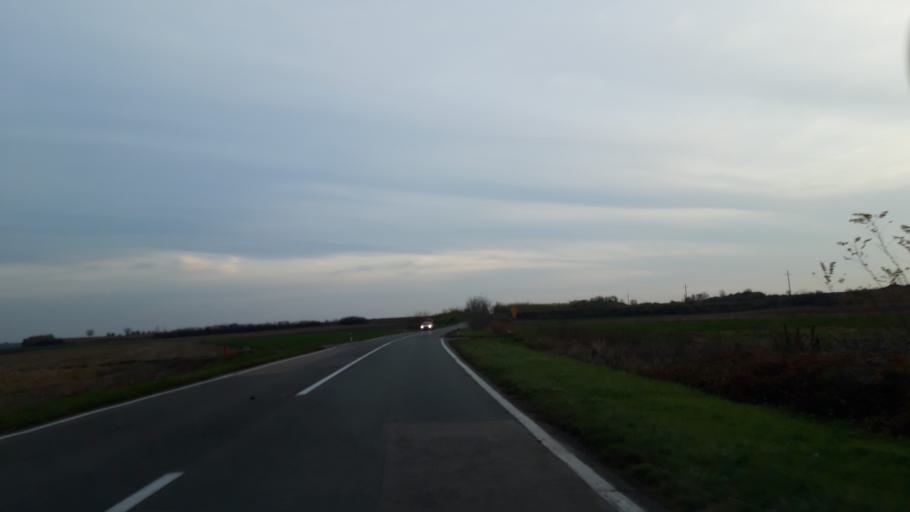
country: RS
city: Ostojicevo
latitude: 45.9070
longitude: 20.1540
